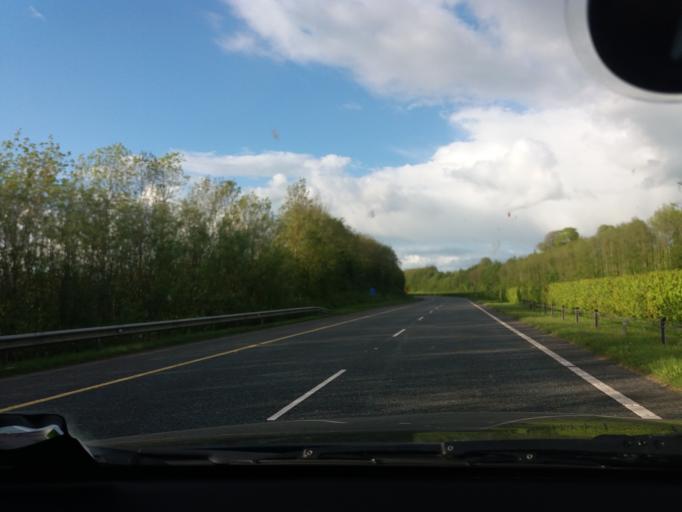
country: IE
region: Leinster
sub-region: Kildare
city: Kilcullen
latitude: 53.1468
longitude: -6.7567
